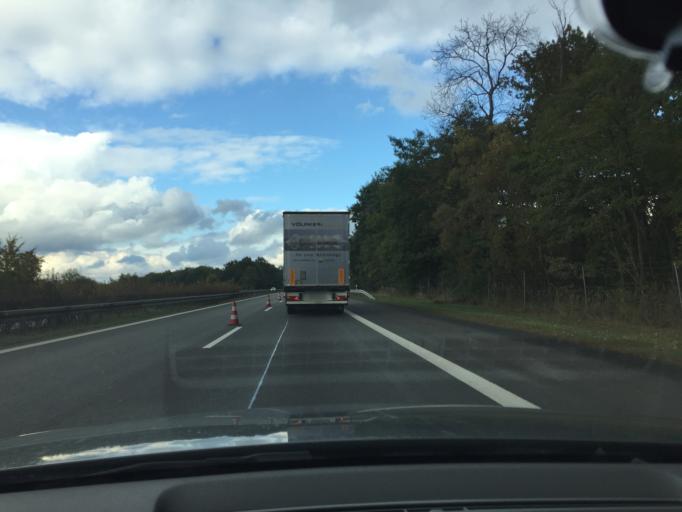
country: DE
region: Brandenburg
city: Bronkow
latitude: 51.6270
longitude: 13.9433
